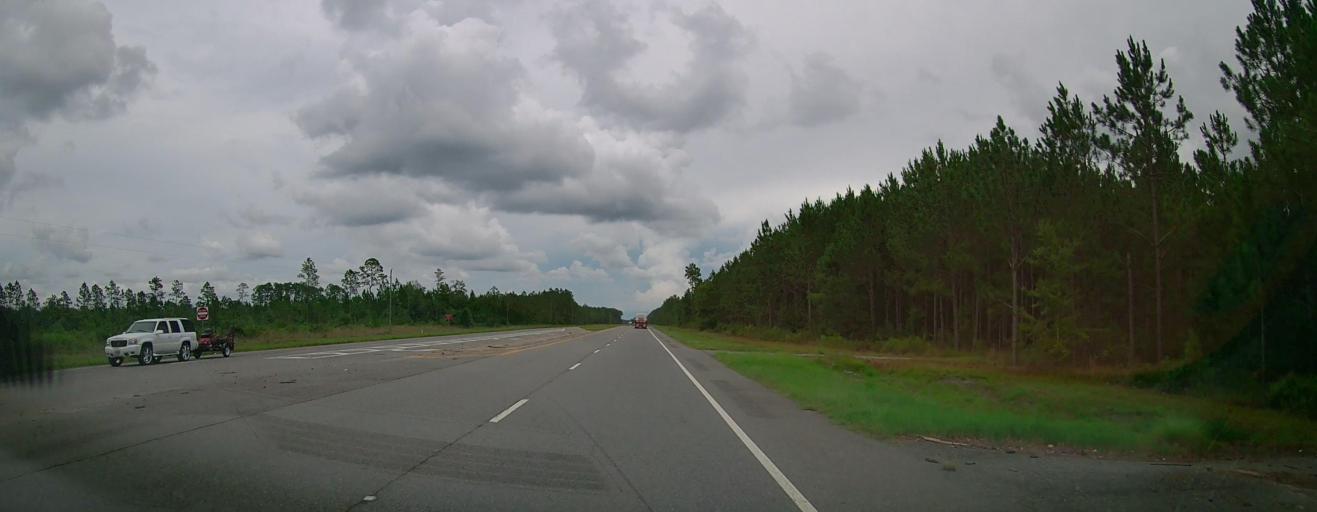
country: US
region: Georgia
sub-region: Wayne County
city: Jesup
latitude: 31.6743
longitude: -82.0696
